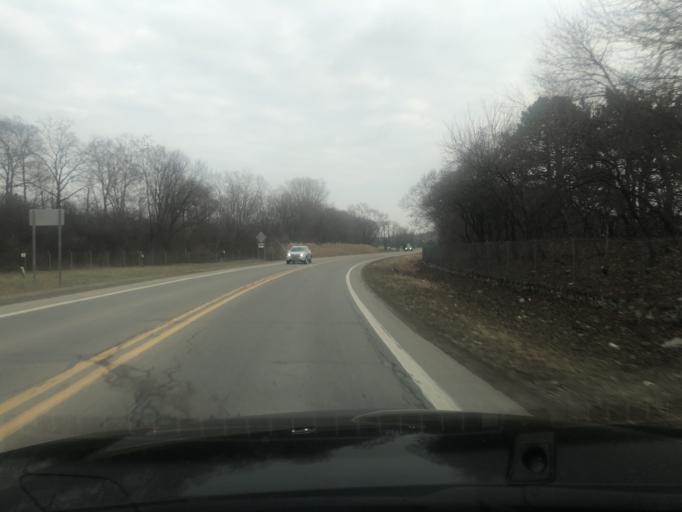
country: US
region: Michigan
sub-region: Wayne County
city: Belleville
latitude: 42.2209
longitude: -83.5188
